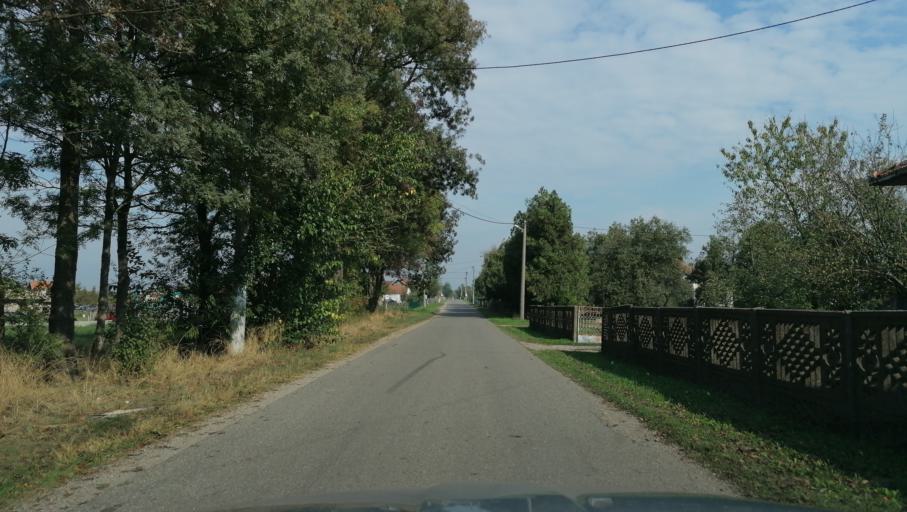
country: BA
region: Republika Srpska
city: Popovi
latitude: 44.7764
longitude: 19.2715
